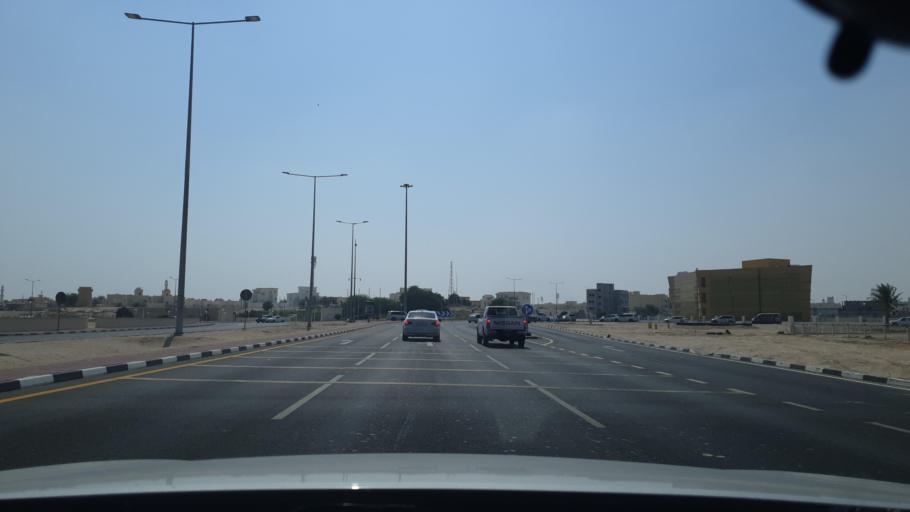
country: QA
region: Al Khawr
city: Al Khawr
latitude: 25.6920
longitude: 51.5005
